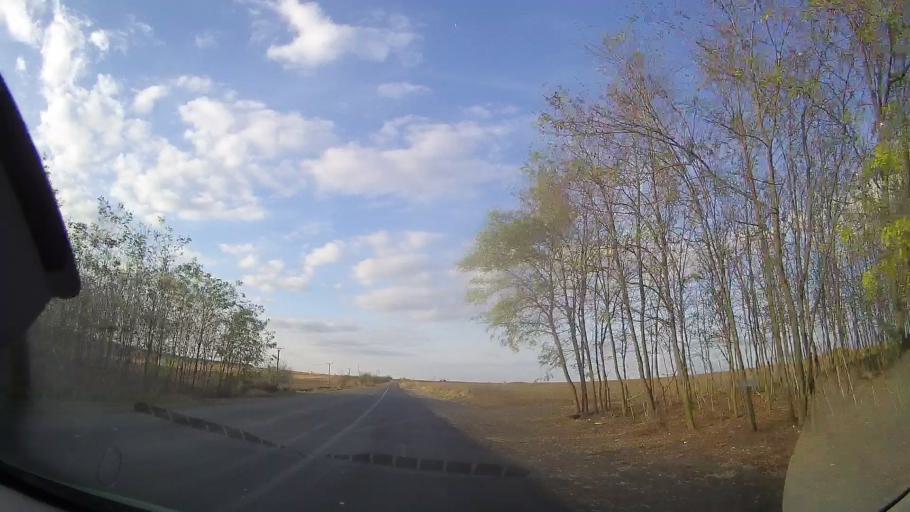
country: RO
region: Constanta
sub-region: Comuna Dumbraveni
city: Dumbraveni
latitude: 43.9284
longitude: 28.0296
